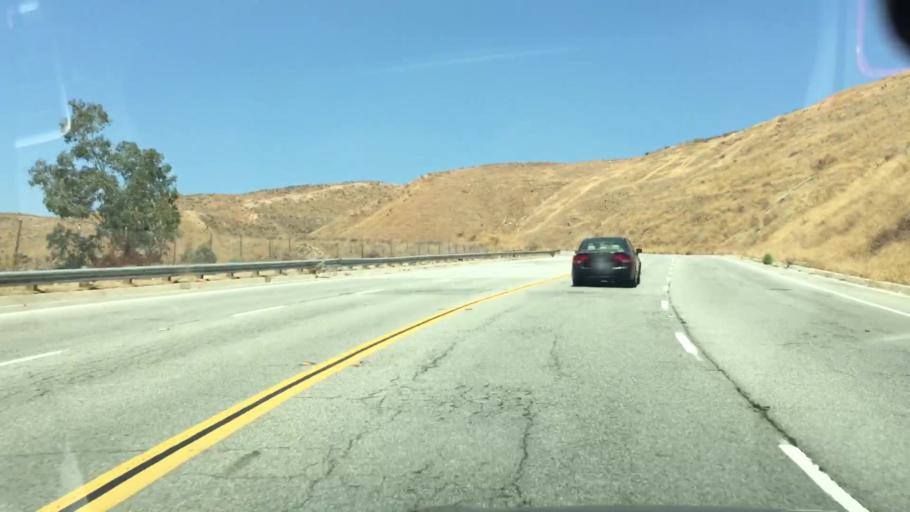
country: US
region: California
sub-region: San Bernardino County
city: Muscoy
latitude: 34.1560
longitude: -117.3217
